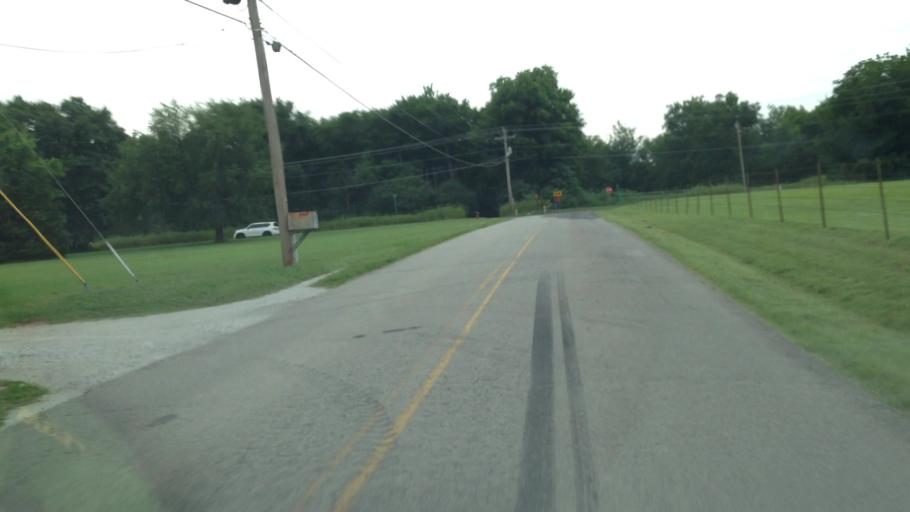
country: US
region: Oklahoma
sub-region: Delaware County
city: Cleora
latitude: 36.5528
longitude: -94.9617
